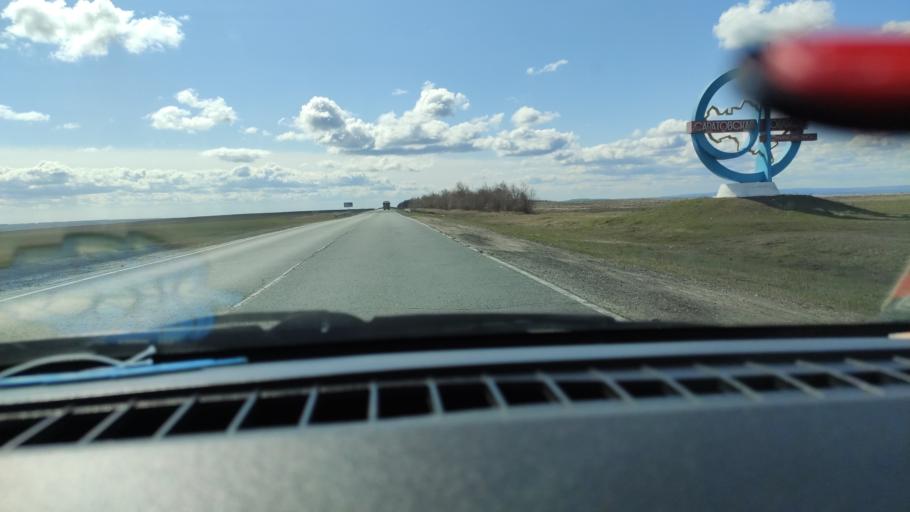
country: RU
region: Saratov
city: Dukhovnitskoye
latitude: 52.7974
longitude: 48.2309
